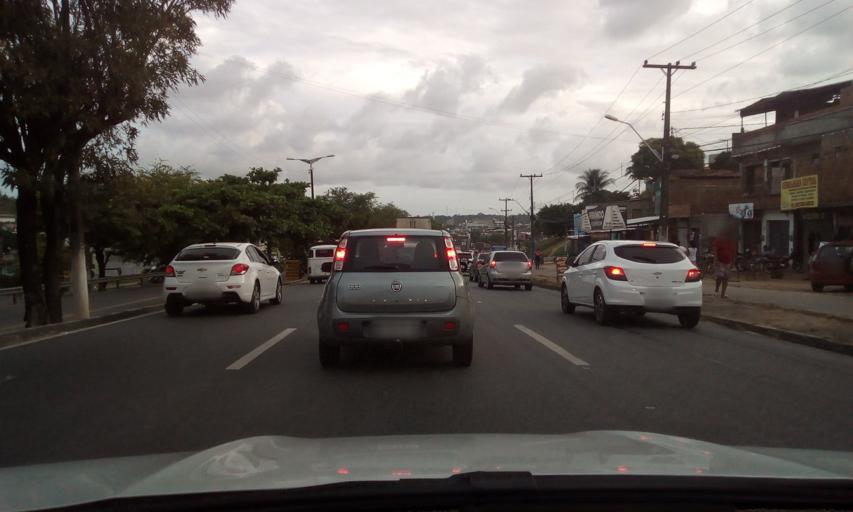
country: BR
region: Pernambuco
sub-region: Abreu E Lima
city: Abreu e Lima
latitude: -7.9016
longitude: -34.9018
